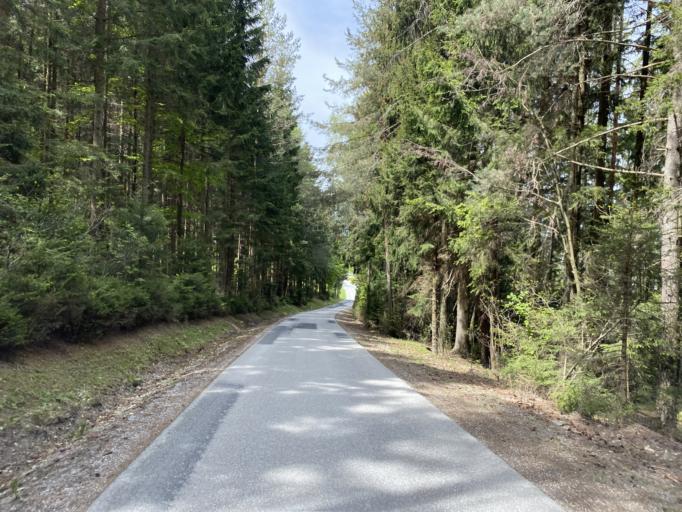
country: AT
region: Styria
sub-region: Politischer Bezirk Weiz
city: Gschaid bei Birkfeld
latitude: 47.3598
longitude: 15.7347
